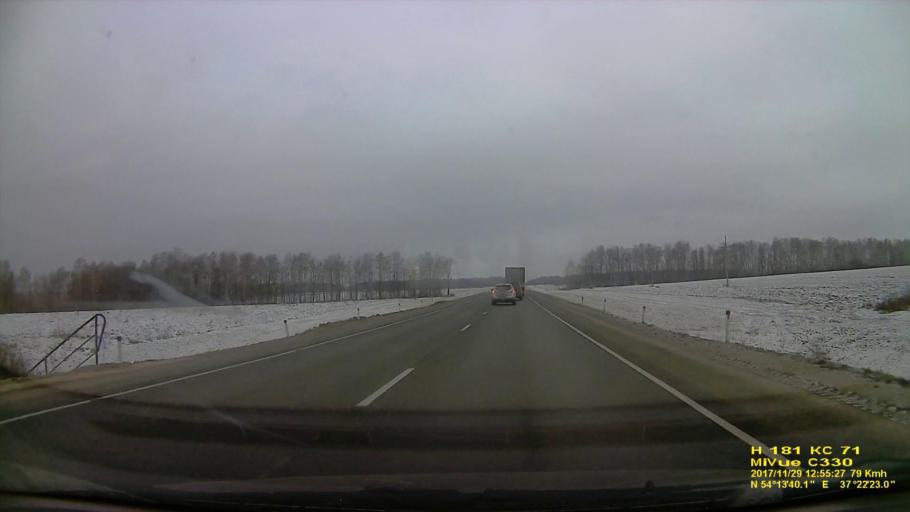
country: RU
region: Tula
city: Leninskiy
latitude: 54.2279
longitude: 37.3729
